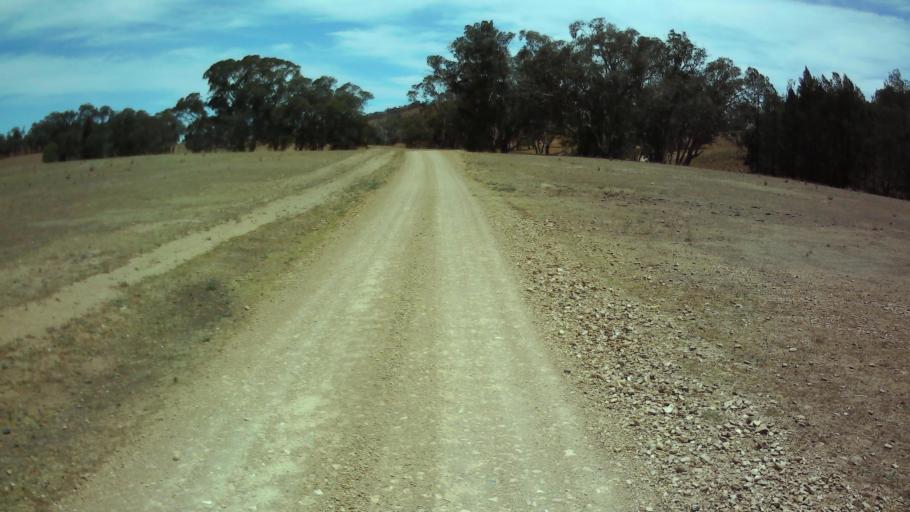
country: AU
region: New South Wales
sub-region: Weddin
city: Grenfell
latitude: -33.7432
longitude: 148.1745
